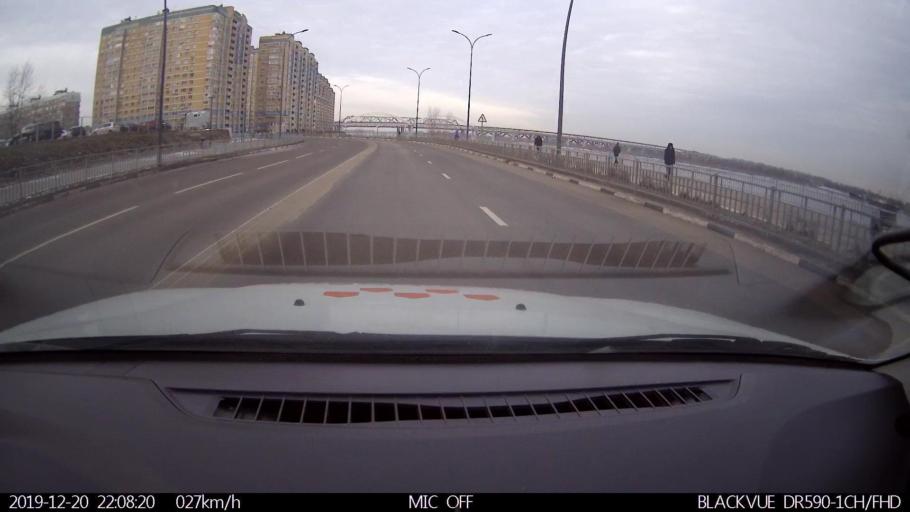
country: RU
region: Nizjnij Novgorod
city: Nizhniy Novgorod
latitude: 56.3464
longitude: 43.9400
